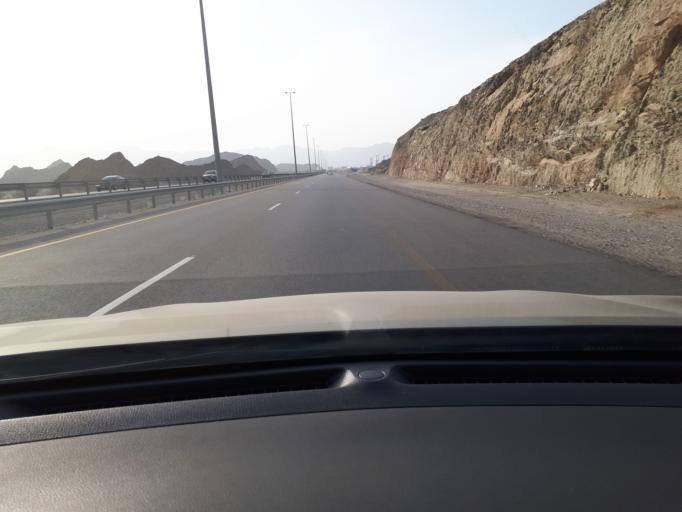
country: OM
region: Muhafazat Masqat
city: Bawshar
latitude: 23.4571
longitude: 58.5016
